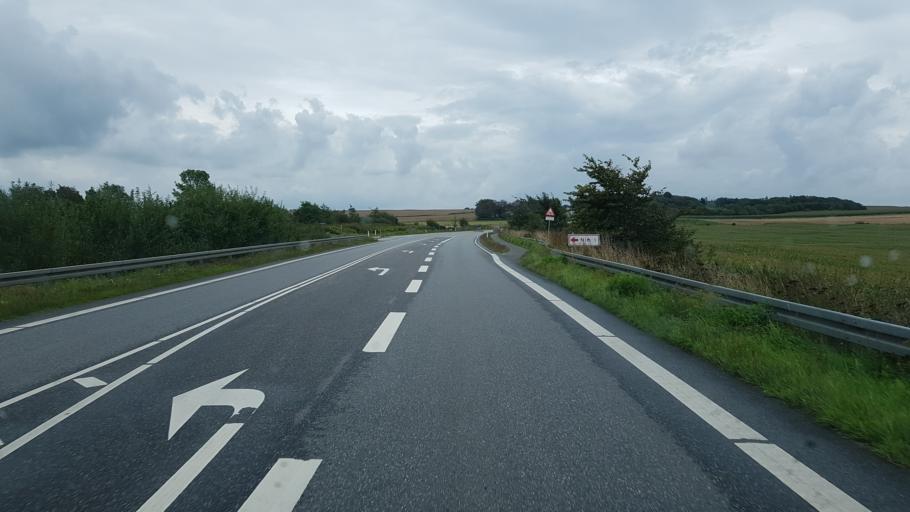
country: DK
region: Central Jutland
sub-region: Horsens Kommune
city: Braedstrup
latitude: 55.9190
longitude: 9.6937
